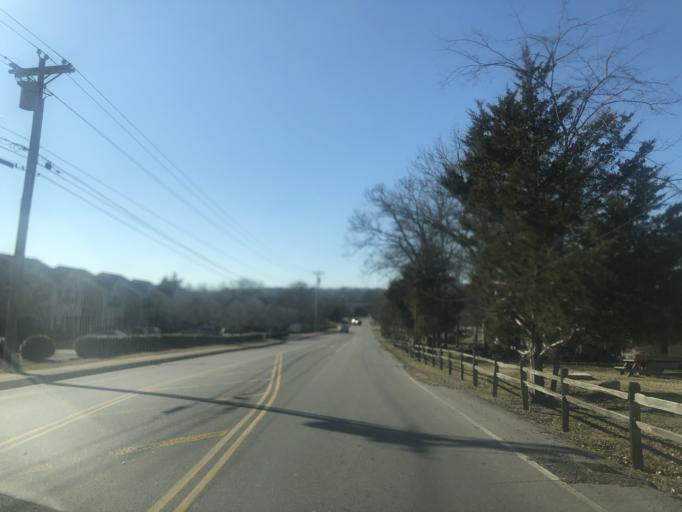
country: US
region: Tennessee
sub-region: Rutherford County
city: Smyrna
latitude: 35.9670
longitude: -86.5292
